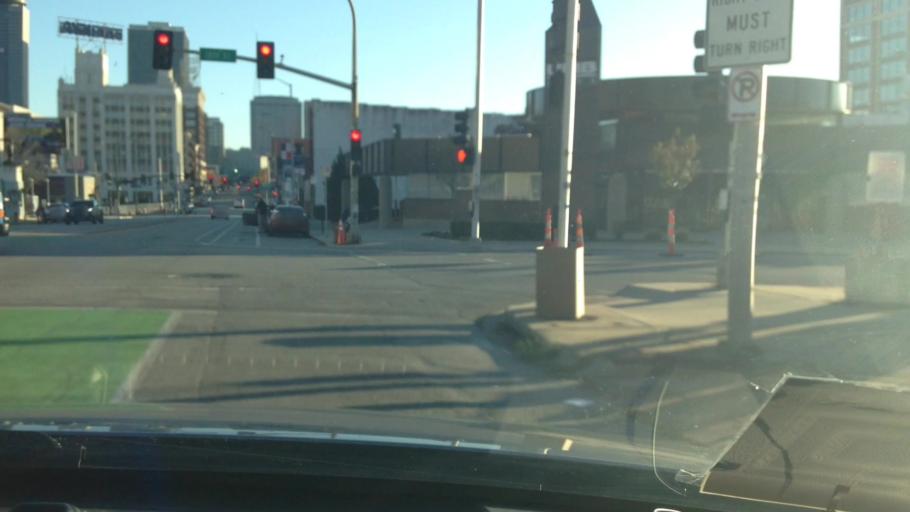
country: US
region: Missouri
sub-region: Jackson County
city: Kansas City
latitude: 39.0919
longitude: -94.5814
